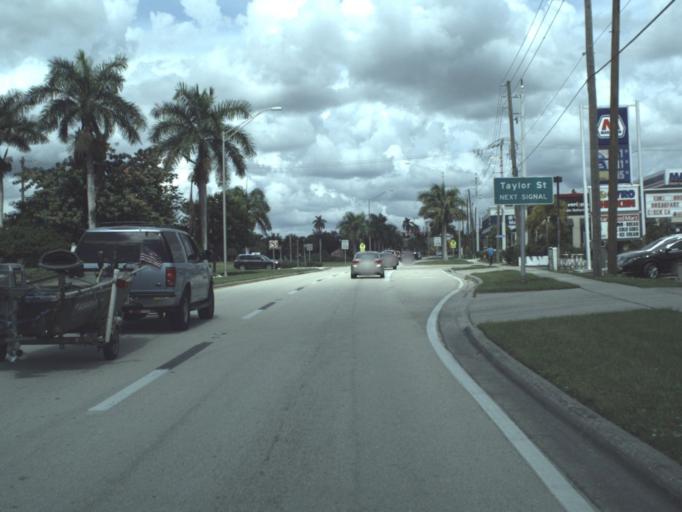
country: US
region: Florida
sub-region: Charlotte County
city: Punta Gorda
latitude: 26.9290
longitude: -82.0473
